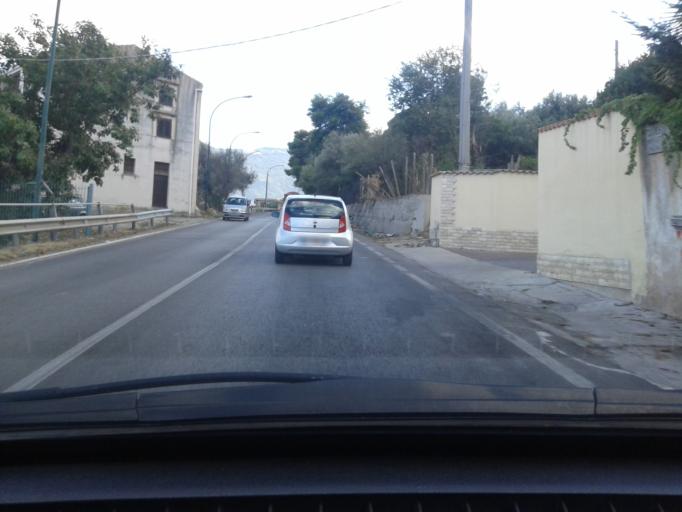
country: IT
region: Sicily
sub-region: Palermo
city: Monreale
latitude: 38.0852
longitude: 13.3009
